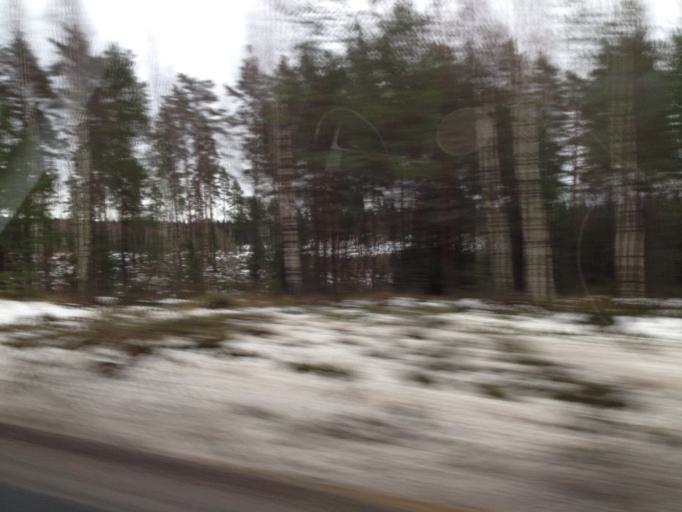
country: FI
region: Uusimaa
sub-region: Raaseporin
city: Pohja
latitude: 60.0130
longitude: 23.5540
